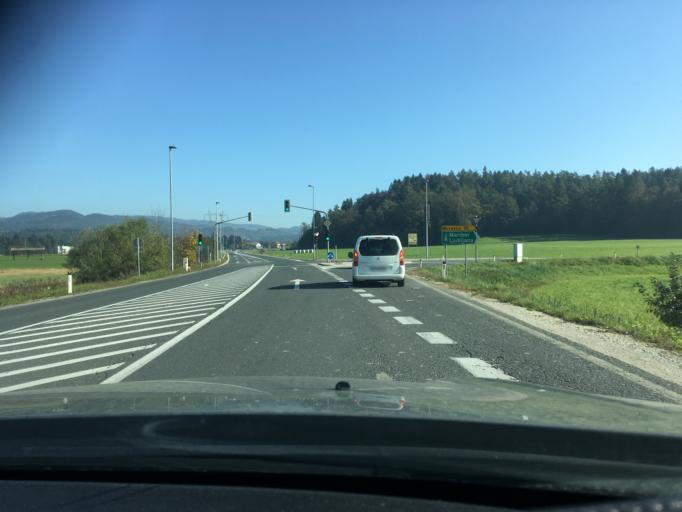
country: SI
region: Domzale
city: Dob
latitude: 46.1585
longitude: 14.6439
